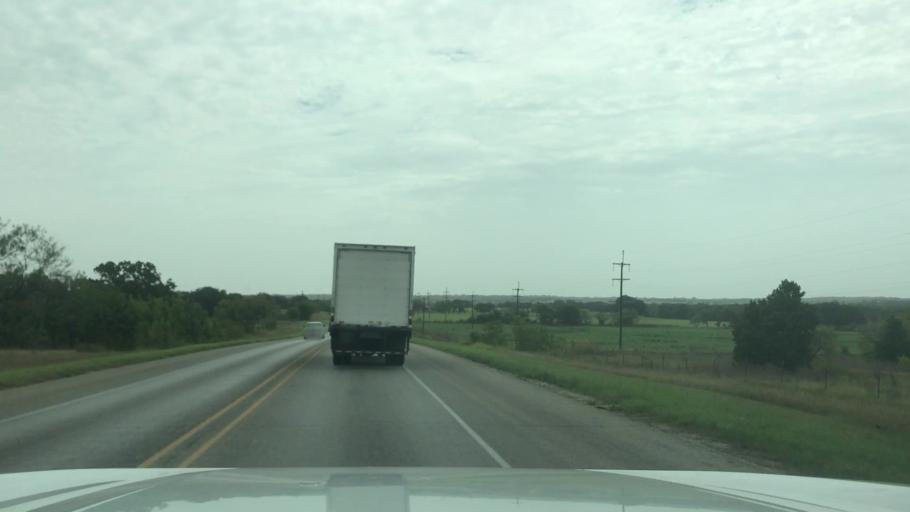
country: US
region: Texas
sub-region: Comanche County
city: De Leon
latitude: 32.1000
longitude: -98.4724
